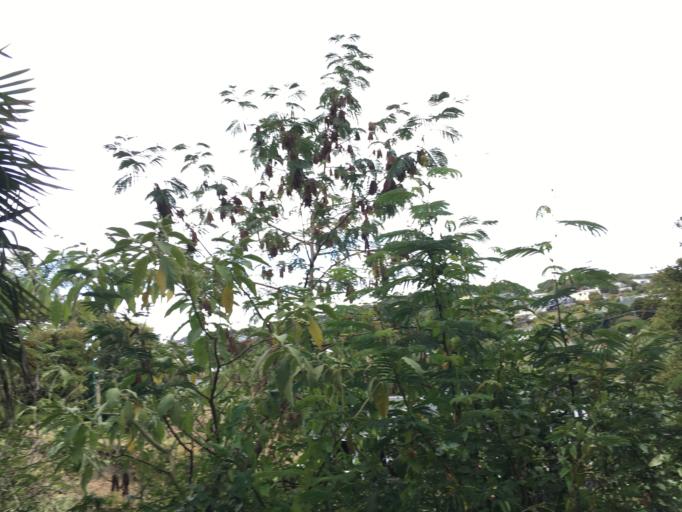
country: NZ
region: Auckland
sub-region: Auckland
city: Pakuranga
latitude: -36.7928
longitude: 175.0210
